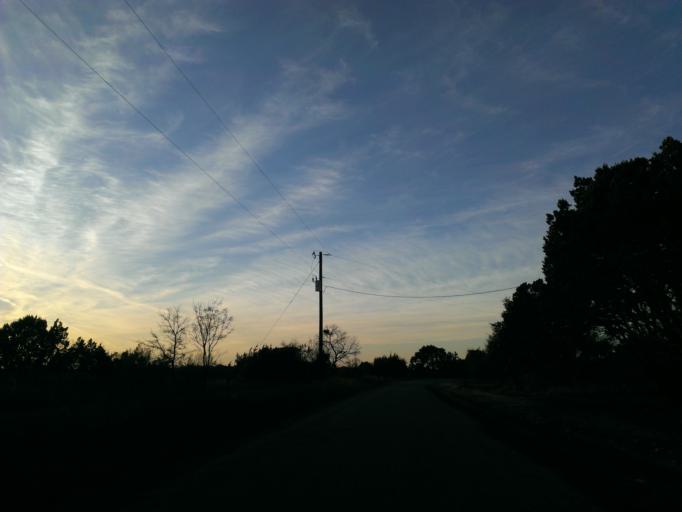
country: US
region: Texas
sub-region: Burnet County
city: Bertram
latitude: 30.7233
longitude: -98.0787
